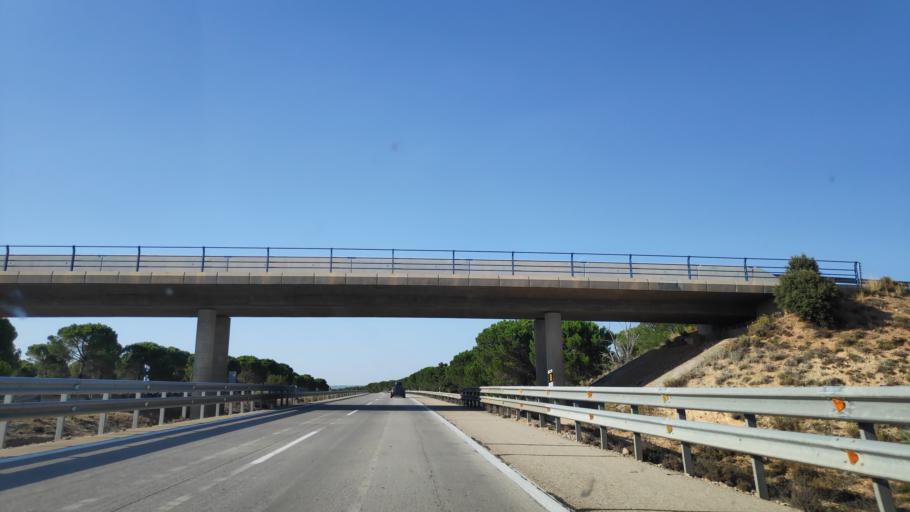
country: ES
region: Castille-La Mancha
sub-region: Provincia de Cuenca
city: Pozoamargo
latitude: 39.3308
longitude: -2.2006
